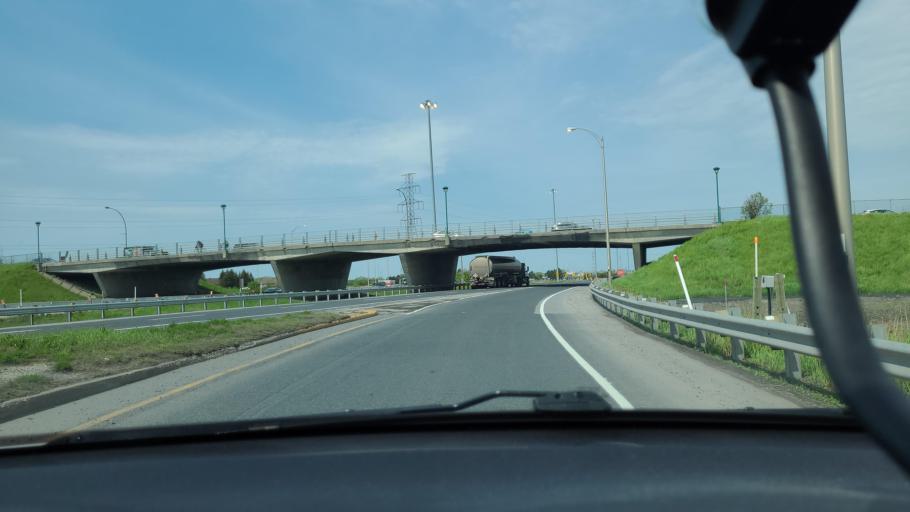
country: CA
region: Quebec
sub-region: Monteregie
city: Boucherville
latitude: 45.5732
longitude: -73.4460
